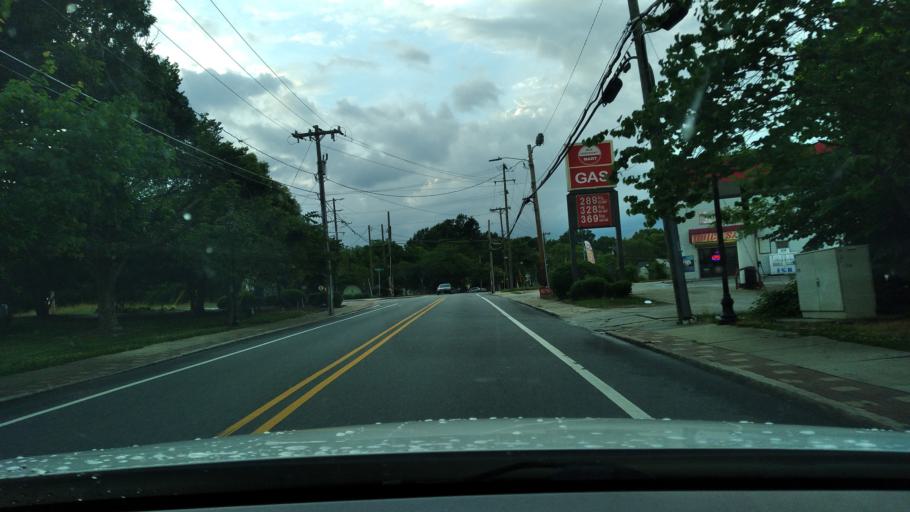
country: US
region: North Carolina
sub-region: Guilford County
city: Greensboro
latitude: 36.0556
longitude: -79.7841
